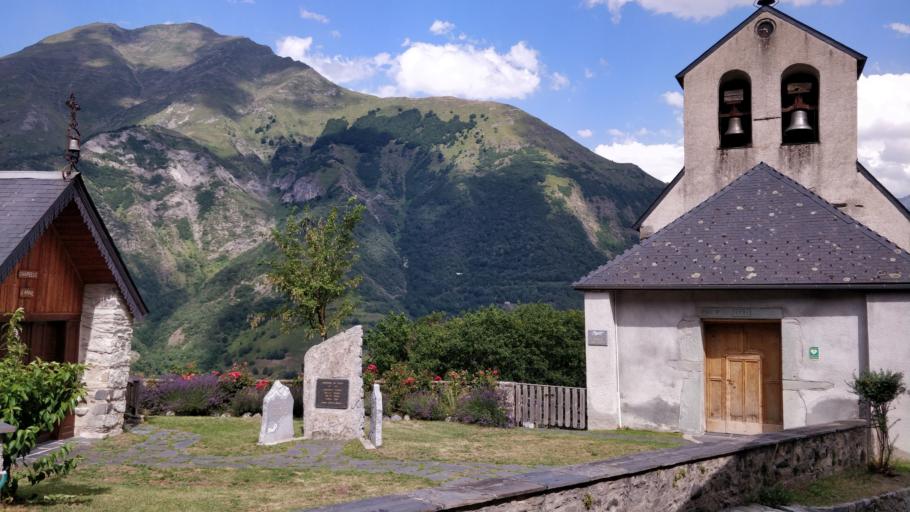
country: FR
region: Midi-Pyrenees
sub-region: Departement des Hautes-Pyrenees
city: Luz-Saint-Sauveur
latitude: 42.8888
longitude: -0.0314
